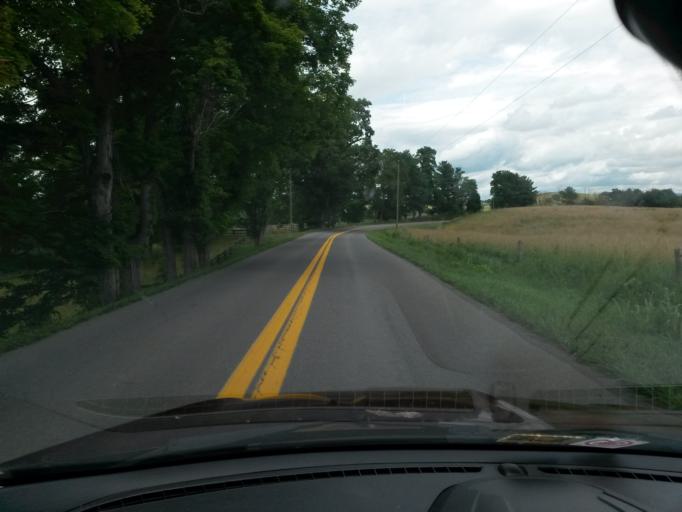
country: US
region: West Virginia
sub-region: Monroe County
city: Union
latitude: 37.5479
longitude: -80.5319
